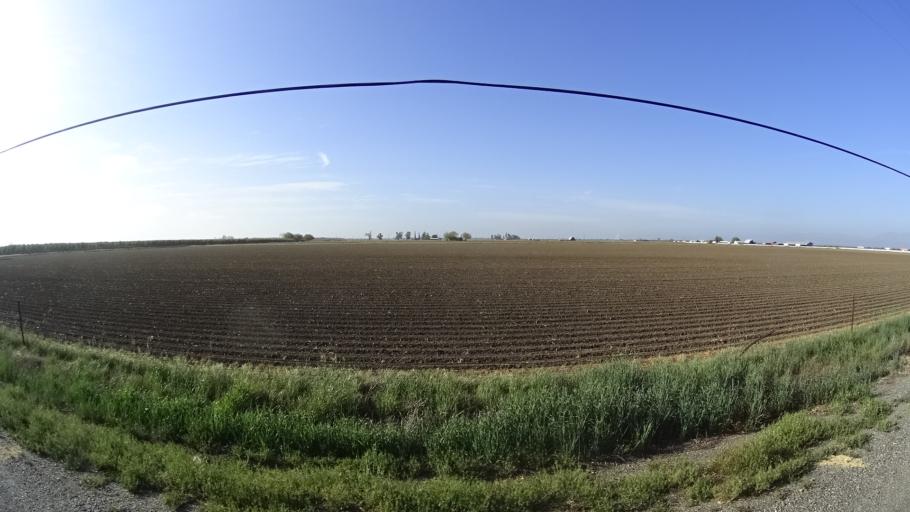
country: US
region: California
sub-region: Glenn County
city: Willows
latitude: 39.5824
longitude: -122.2007
